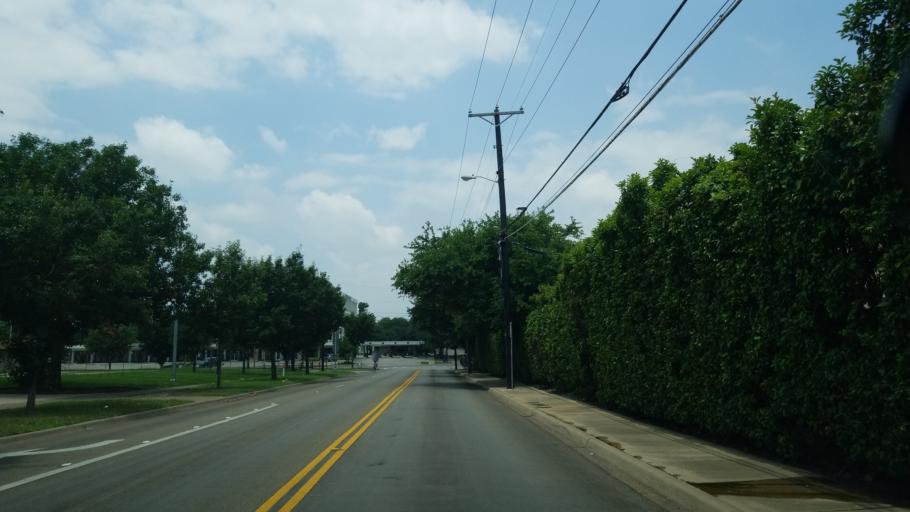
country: US
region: Texas
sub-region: Dallas County
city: University Park
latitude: 32.8493
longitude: -96.8198
